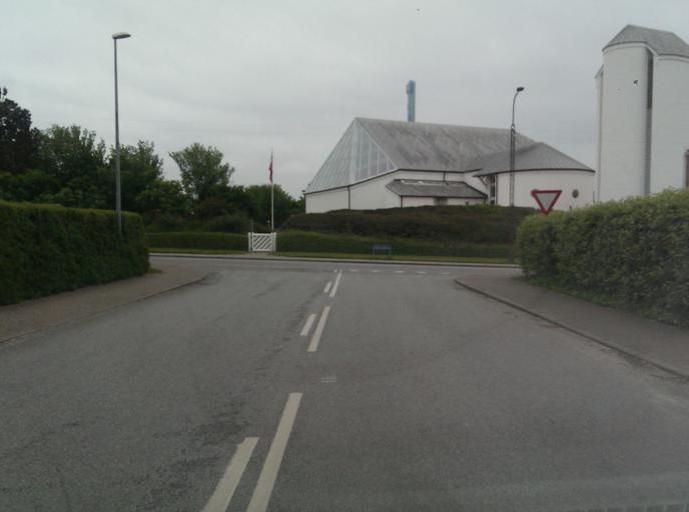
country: DK
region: South Denmark
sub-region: Fano Kommune
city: Nordby
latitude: 55.5261
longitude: 8.3560
